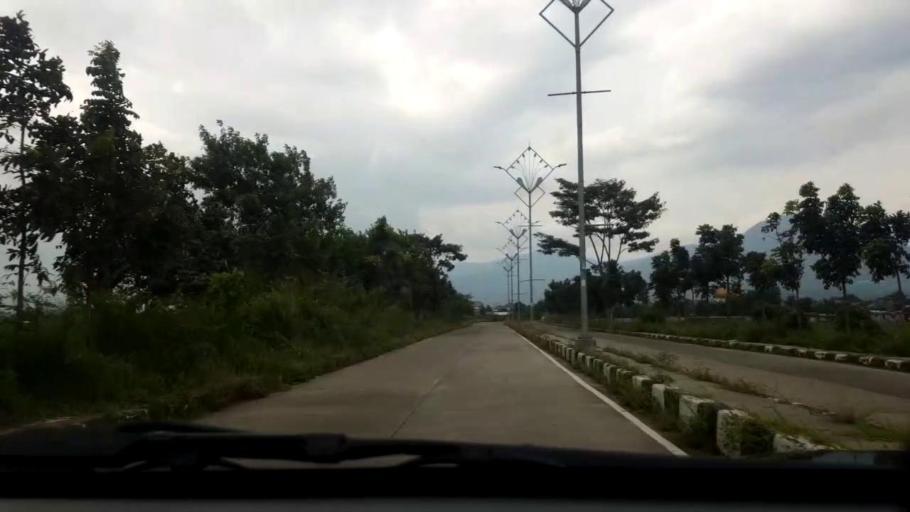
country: ID
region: West Java
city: Cileunyi
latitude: -6.9515
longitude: 107.7110
